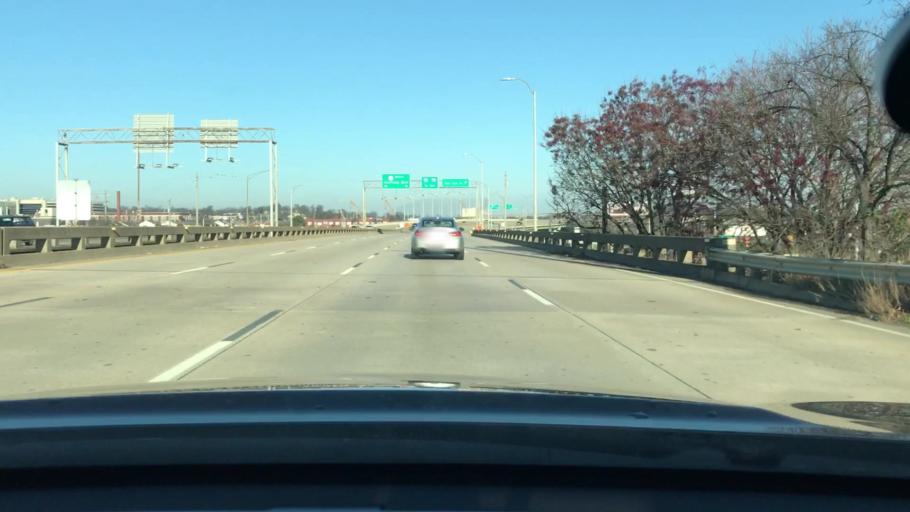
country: US
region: Alabama
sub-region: Jefferson County
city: Birmingham
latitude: 33.5180
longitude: -86.7973
